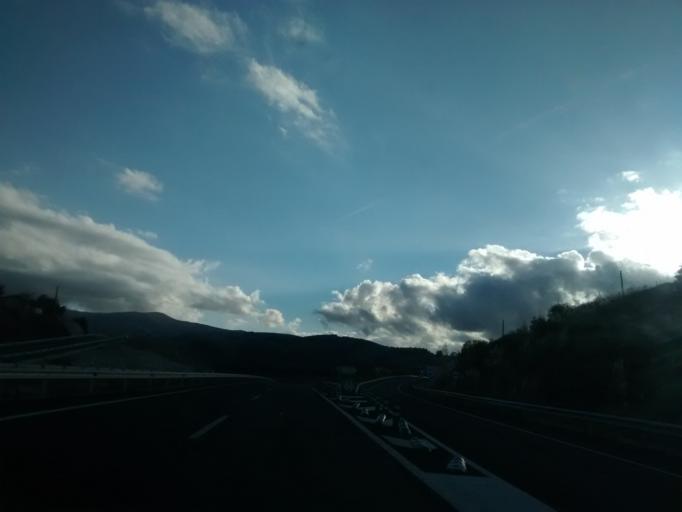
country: ES
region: Cantabria
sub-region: Provincia de Cantabria
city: Lierganes
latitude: 43.3702
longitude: -3.7568
